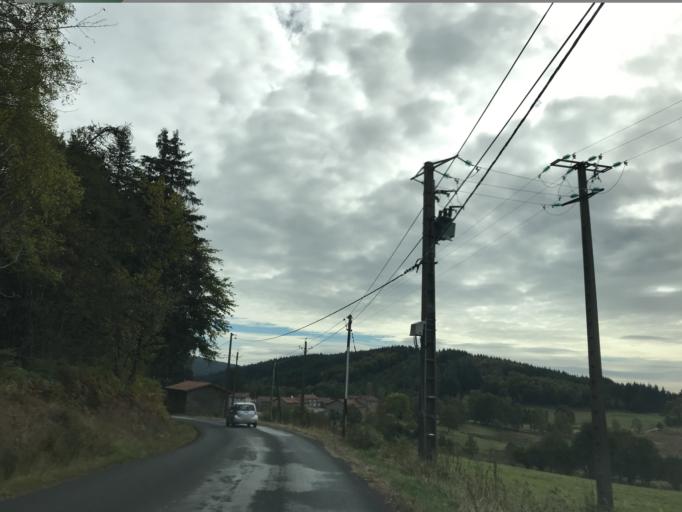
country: FR
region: Auvergne
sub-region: Departement du Puy-de-Dome
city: Celles-sur-Durolle
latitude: 45.7987
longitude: 3.6690
